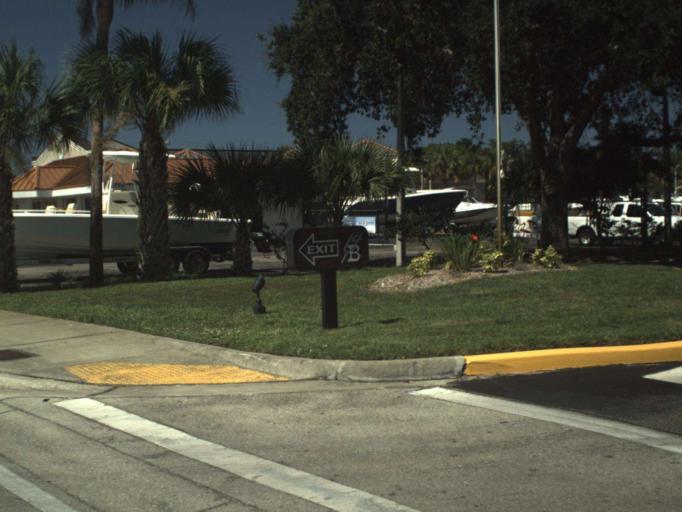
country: US
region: Florida
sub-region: Indian River County
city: Vero Beach
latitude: 27.6287
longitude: -80.3892
